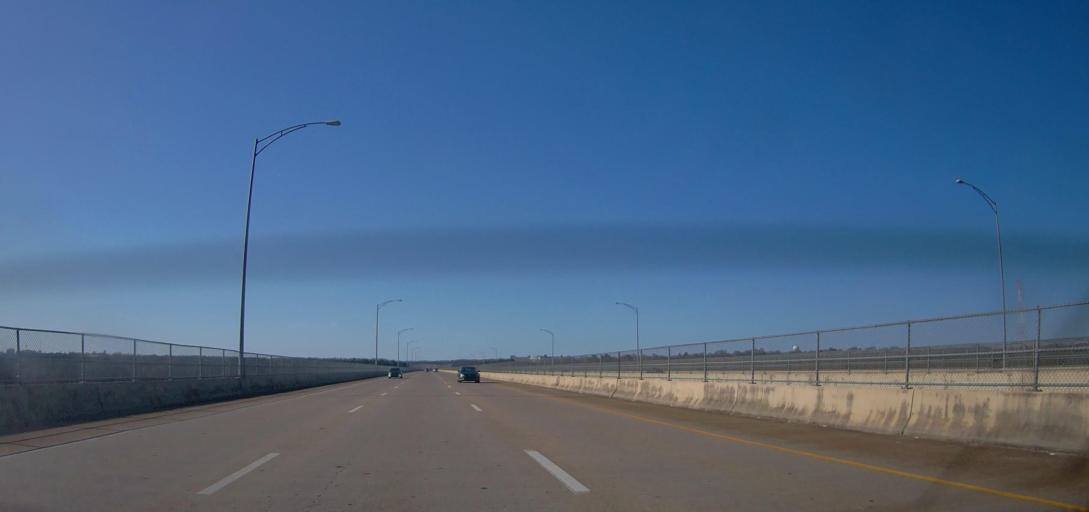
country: US
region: Alabama
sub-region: Lauderdale County
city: East Florence
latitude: 34.7910
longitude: -87.6421
